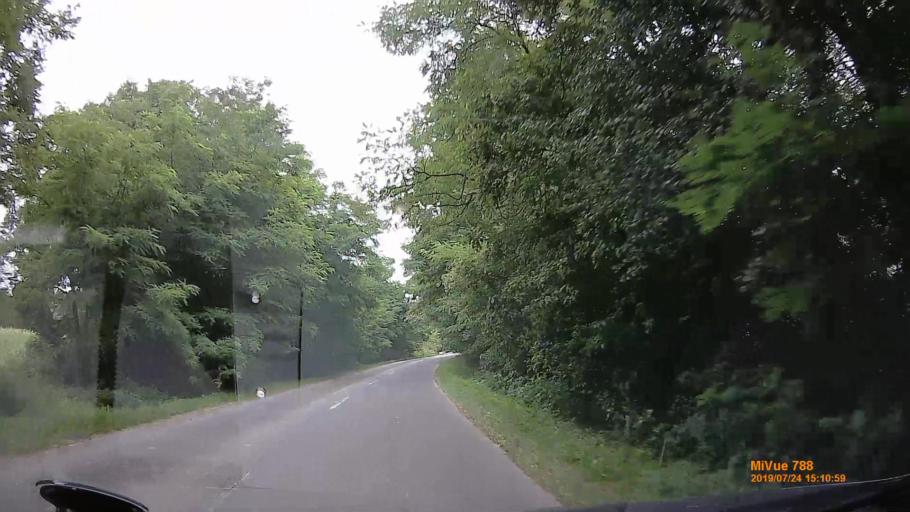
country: HU
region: Szabolcs-Szatmar-Bereg
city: Tarpa
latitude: 48.2032
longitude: 22.4706
